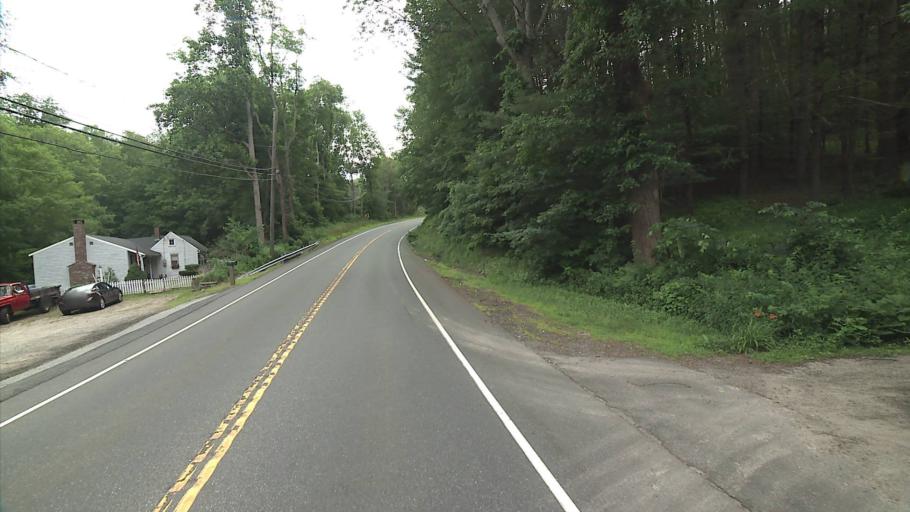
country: US
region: Connecticut
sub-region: New London County
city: Ledyard Center
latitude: 41.4724
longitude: -72.0272
